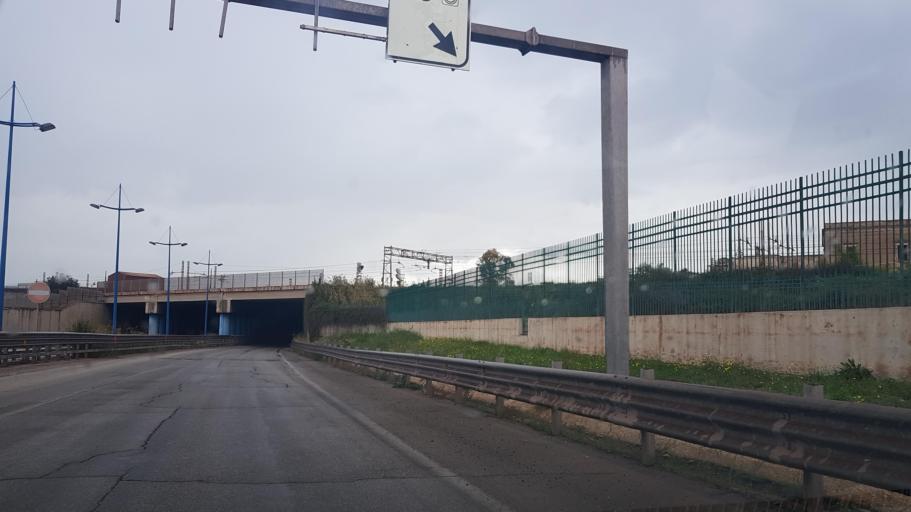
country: IT
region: Apulia
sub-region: Provincia di Taranto
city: Statte
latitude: 40.4813
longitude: 17.2074
